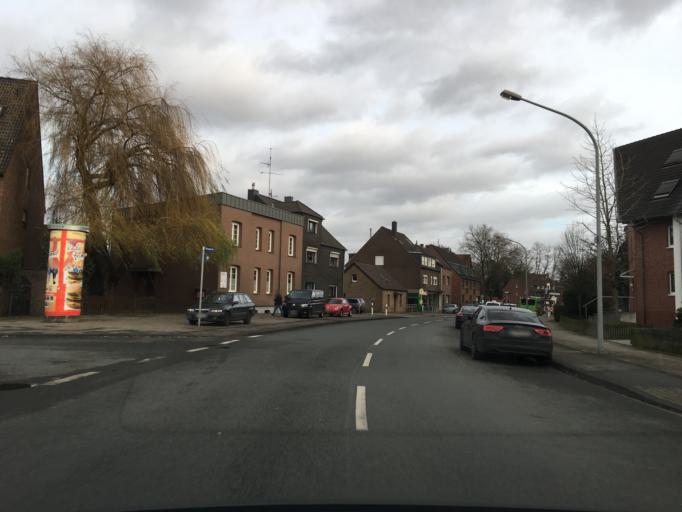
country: DE
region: North Rhine-Westphalia
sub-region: Regierungsbezirk Dusseldorf
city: Oberhausen
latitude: 51.5146
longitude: 6.8232
